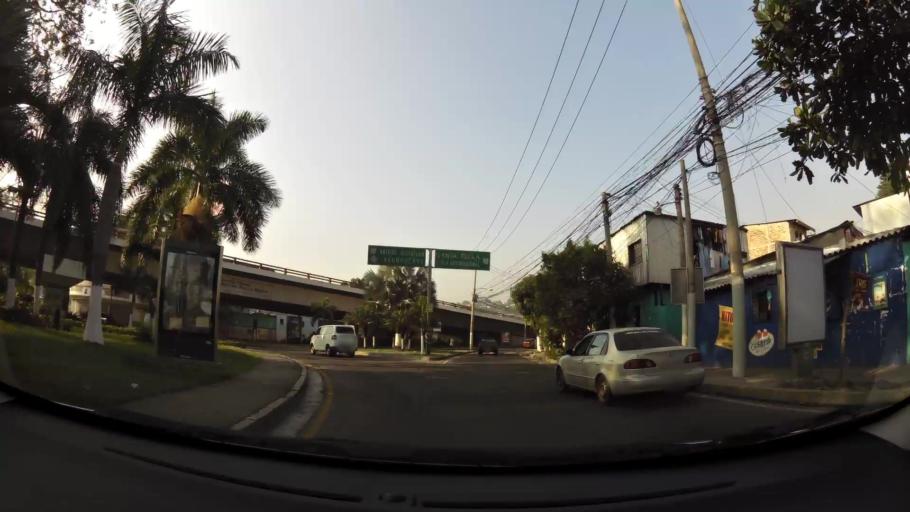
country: SV
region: La Libertad
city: Antiguo Cuscatlan
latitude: 13.6843
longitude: -89.2234
